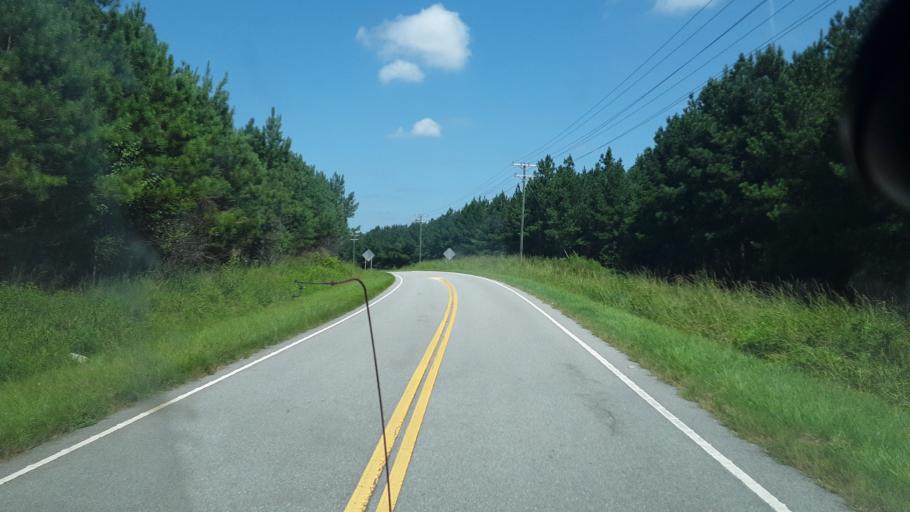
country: US
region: South Carolina
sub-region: Bamberg County
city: Bamberg
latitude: 33.4107
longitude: -81.0166
